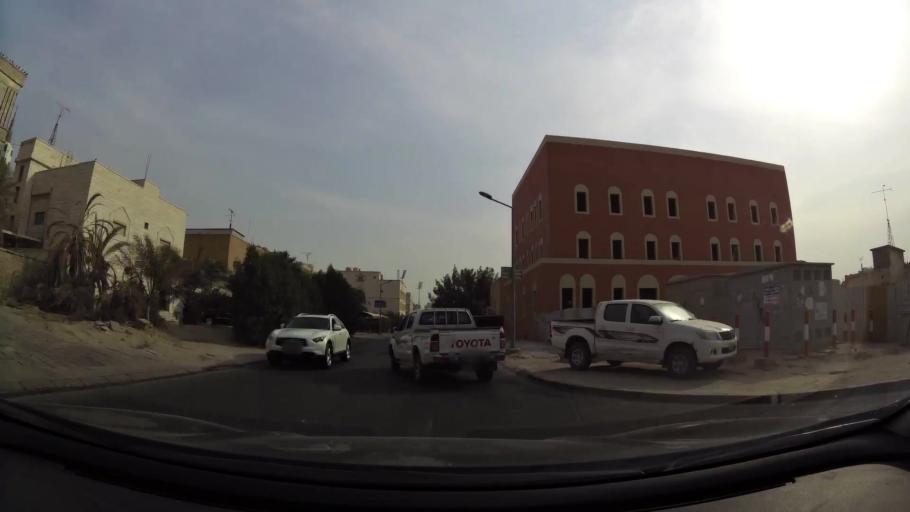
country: KW
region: Al Farwaniyah
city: Al Farwaniyah
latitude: 29.2929
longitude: 47.9627
